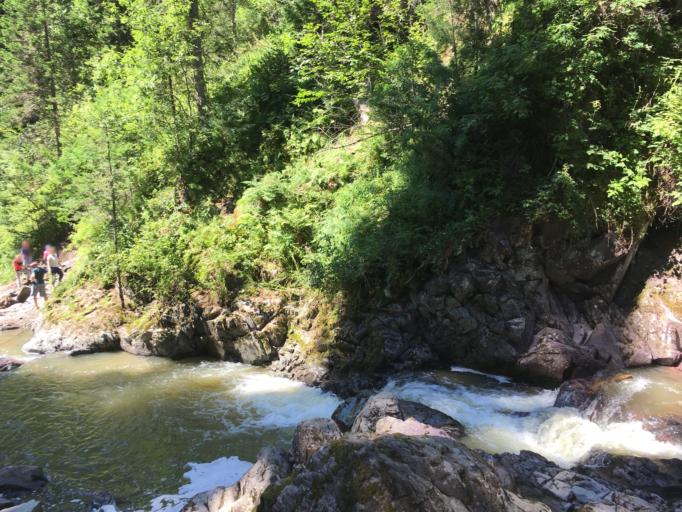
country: RU
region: Altay
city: Artybash
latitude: 51.7919
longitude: 87.3232
